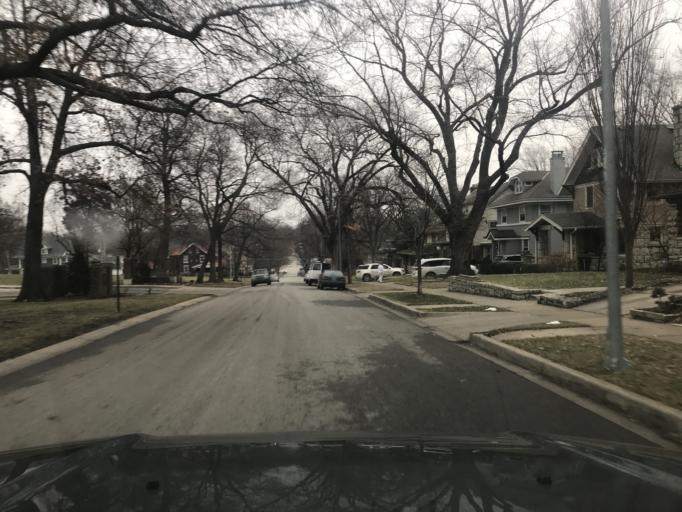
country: US
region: Kansas
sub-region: Johnson County
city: Mission Hills
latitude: 39.0241
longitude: -94.5897
